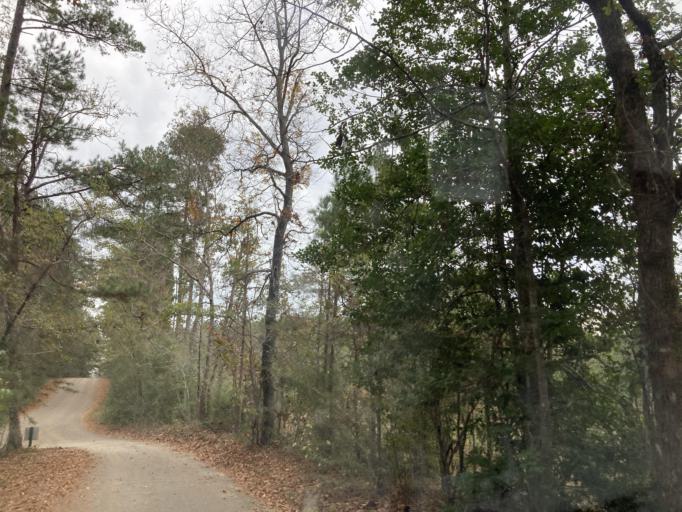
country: US
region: Mississippi
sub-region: Lamar County
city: Lumberton
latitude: 31.0815
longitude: -89.4971
